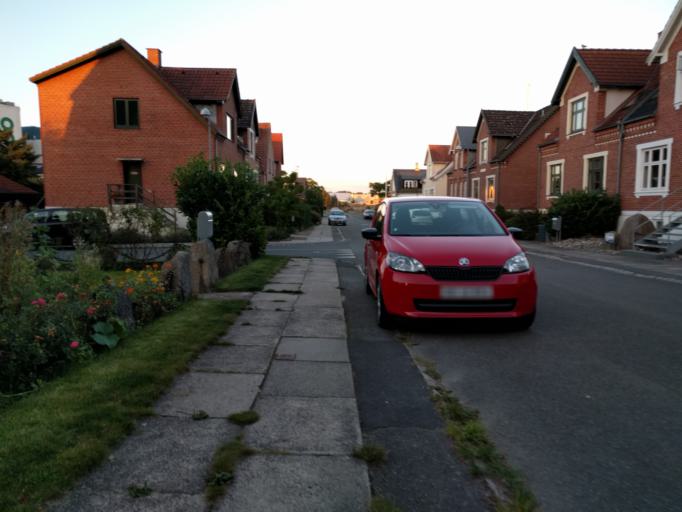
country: DK
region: South Denmark
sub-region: Odense Kommune
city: Odense
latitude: 55.4149
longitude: 10.3763
